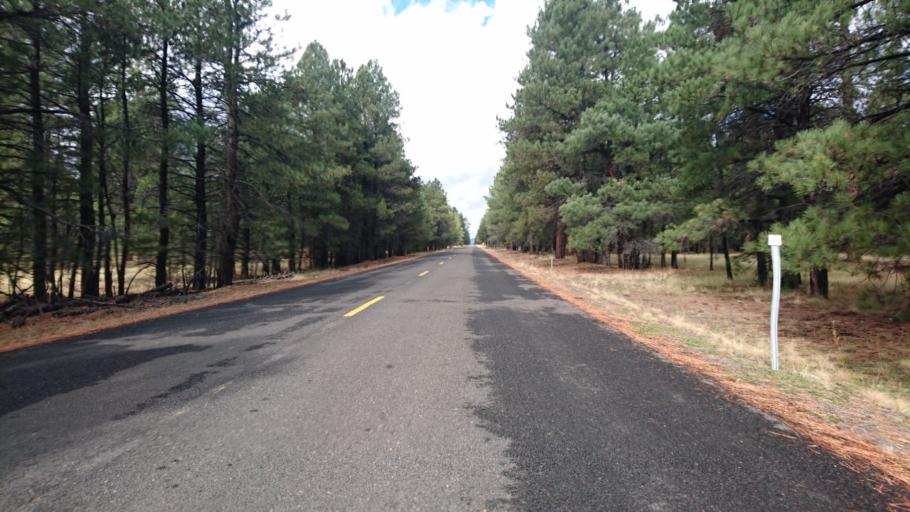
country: US
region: Arizona
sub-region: Coconino County
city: Parks
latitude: 35.2519
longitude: -111.8596
